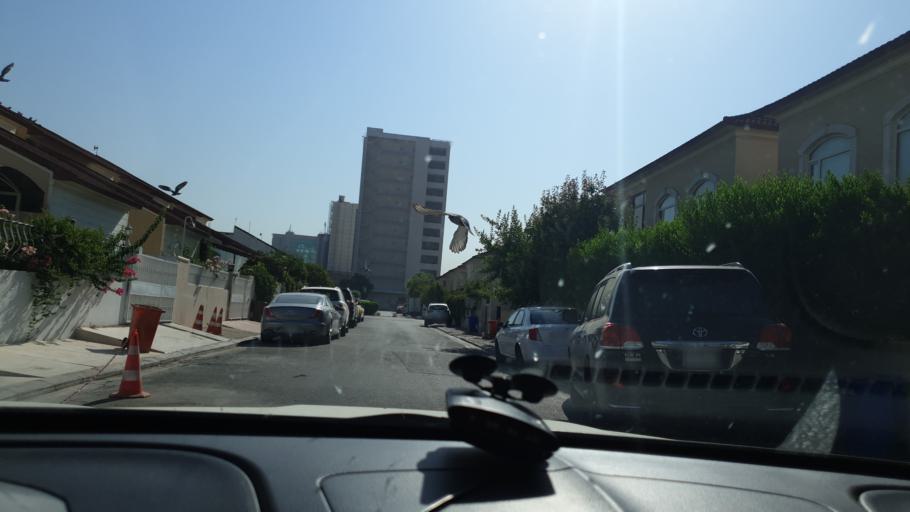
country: IQ
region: Arbil
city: Erbil
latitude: 36.1863
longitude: 43.9686
